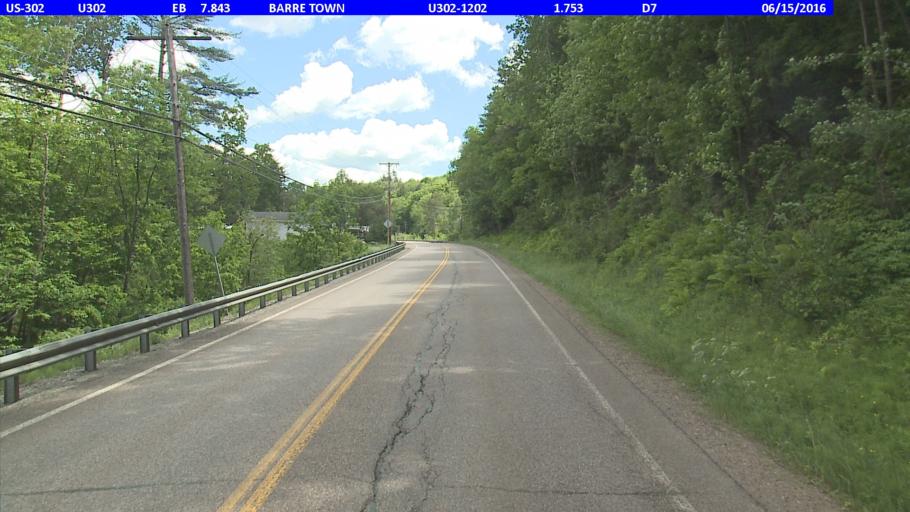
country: US
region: Vermont
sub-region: Washington County
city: South Barre
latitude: 44.1684
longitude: -72.4601
